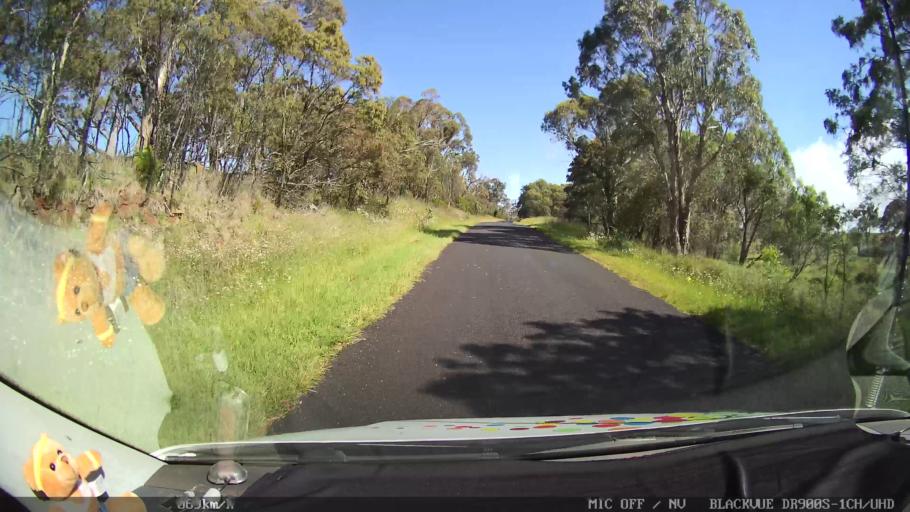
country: AU
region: New South Wales
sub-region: Guyra
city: Guyra
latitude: -30.0646
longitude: 151.6661
